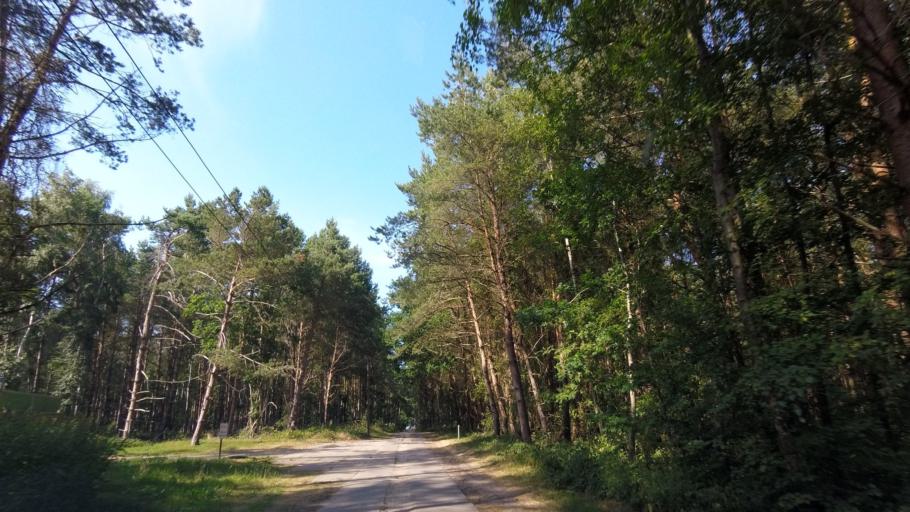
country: DE
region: Mecklenburg-Vorpommern
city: Wiek
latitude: 54.6695
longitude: 13.2970
